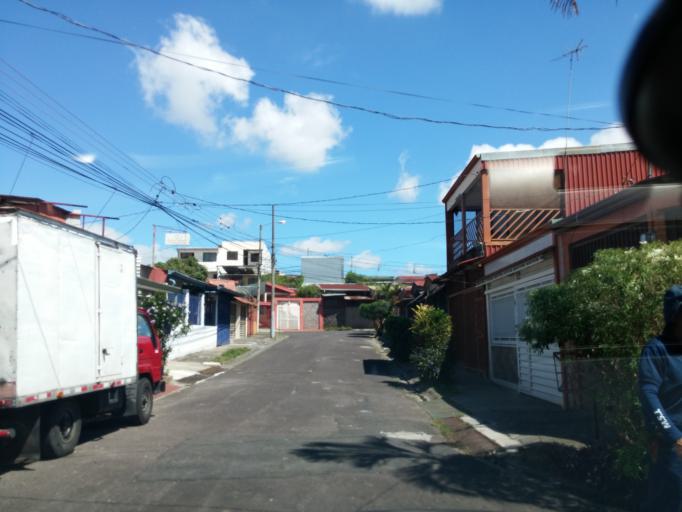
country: CR
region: San Jose
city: San Jose
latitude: 9.9154
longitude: -84.0828
